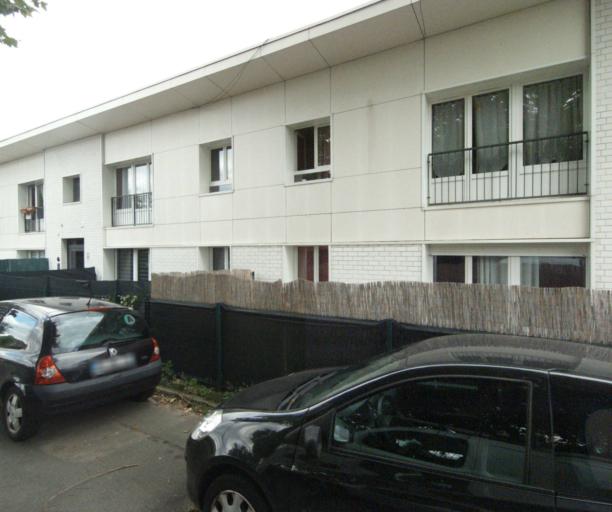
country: FR
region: Nord-Pas-de-Calais
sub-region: Departement du Nord
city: Hem
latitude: 50.6702
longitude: 3.1735
